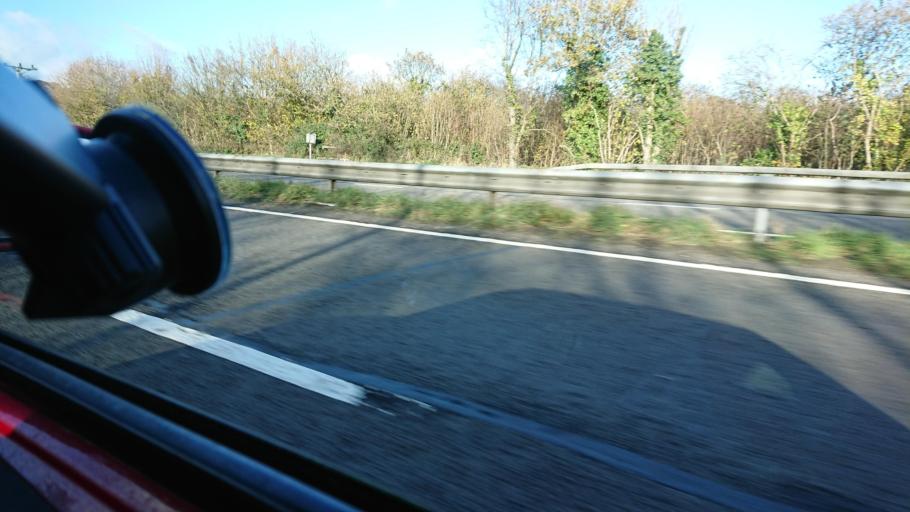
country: GB
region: England
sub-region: Cornwall
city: Saltash
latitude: 50.4155
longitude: -4.2191
